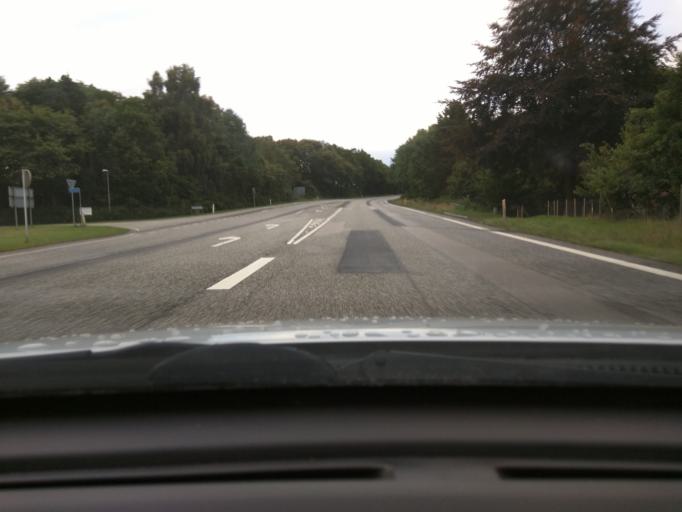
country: DK
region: Central Jutland
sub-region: Viborg Kommune
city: Viborg
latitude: 56.3996
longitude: 9.3734
